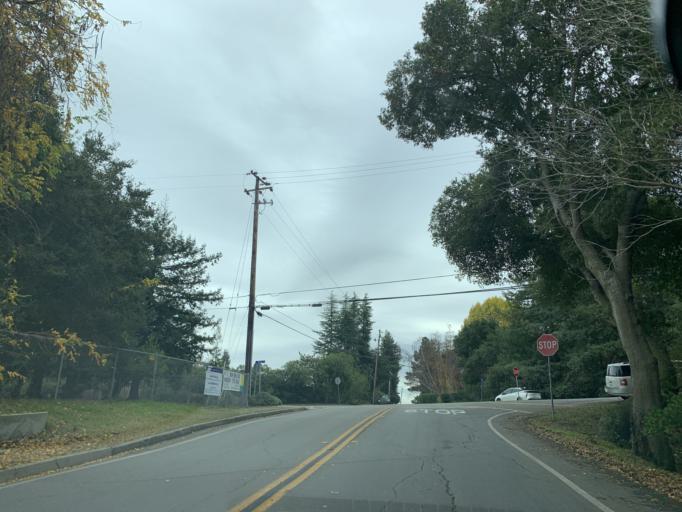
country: US
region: California
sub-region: Santa Clara County
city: Loyola
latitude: 37.3428
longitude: -122.0959
